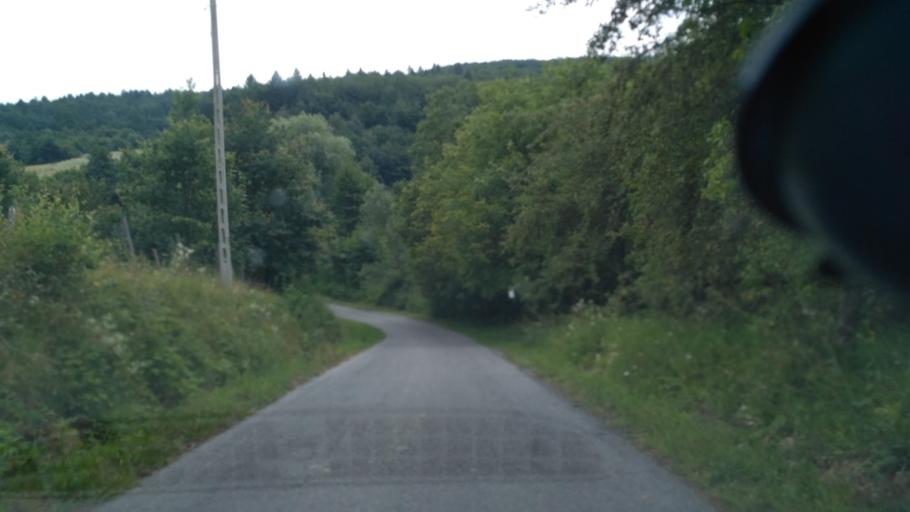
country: PL
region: Subcarpathian Voivodeship
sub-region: Powiat jaroslawski
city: Jodlowka
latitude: 49.8977
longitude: 22.4210
